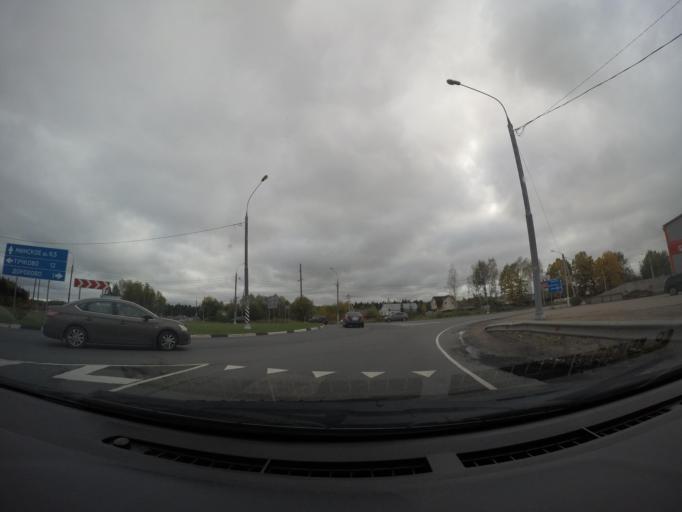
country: RU
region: Moskovskaya
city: Dorokhovo
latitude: 55.5436
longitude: 36.3944
